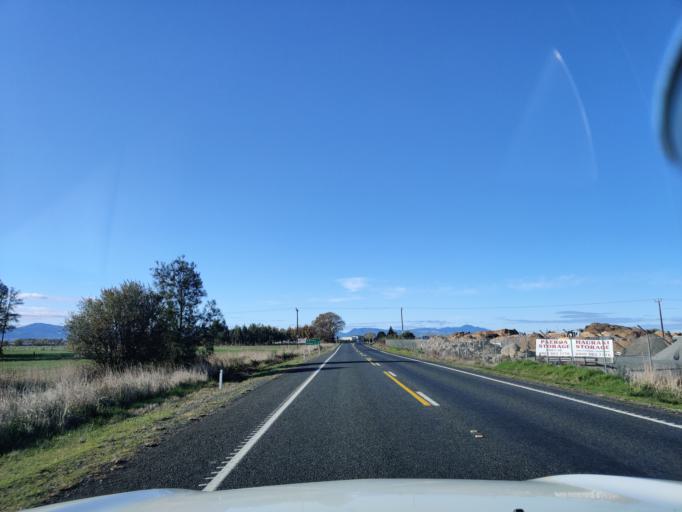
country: NZ
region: Waikato
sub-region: Hauraki District
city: Ngatea
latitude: -37.2955
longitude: 175.5537
